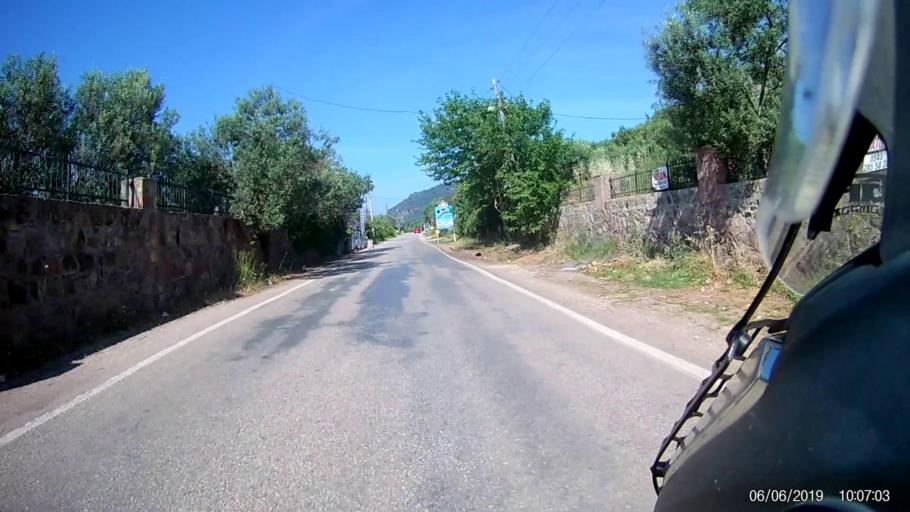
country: TR
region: Canakkale
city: Ayvacik
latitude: 39.5224
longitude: 26.4631
